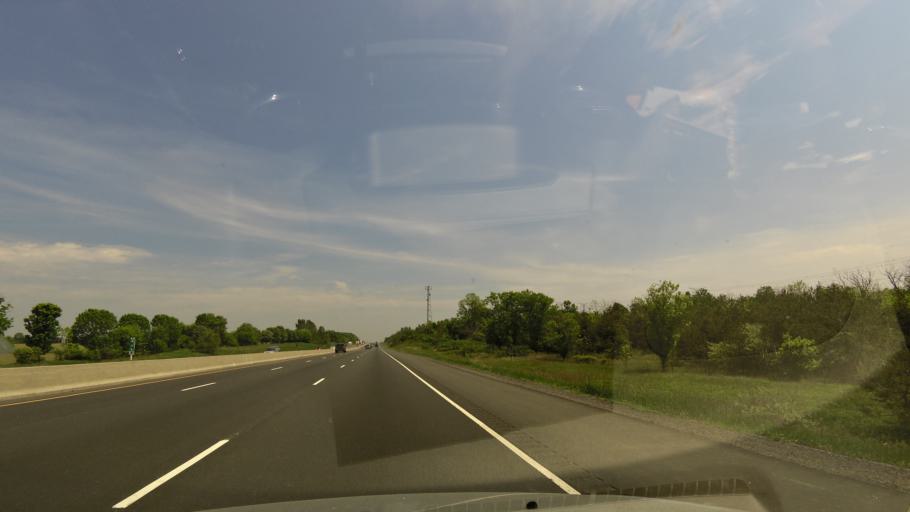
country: CA
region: Ontario
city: Oshawa
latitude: 43.9146
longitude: -78.5654
